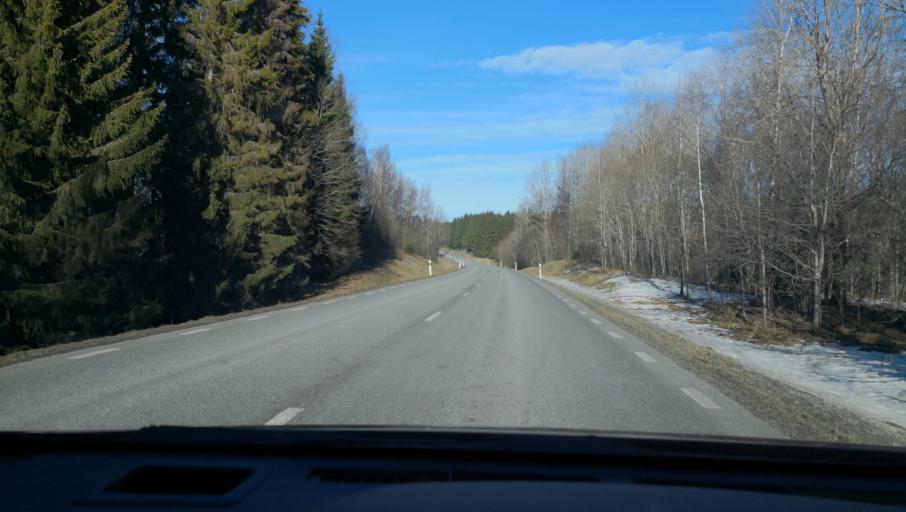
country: SE
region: Uppsala
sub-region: Uppsala Kommun
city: Vattholma
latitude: 60.0262
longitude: 17.7490
